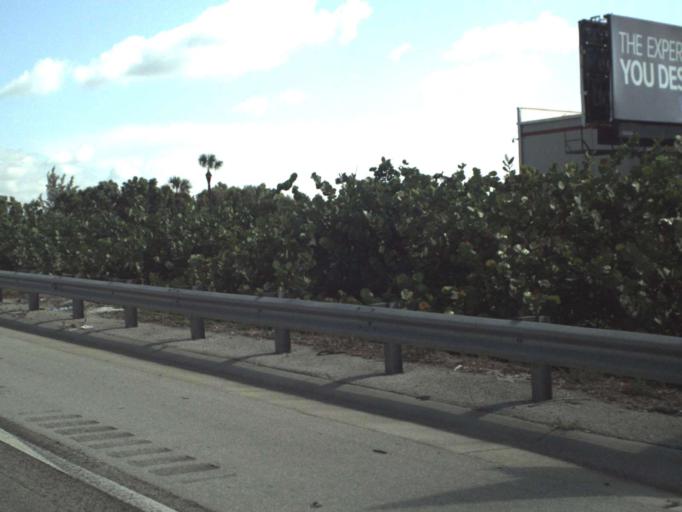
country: US
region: Florida
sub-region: Palm Beach County
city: Mangonia Park
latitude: 26.7682
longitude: -80.0945
